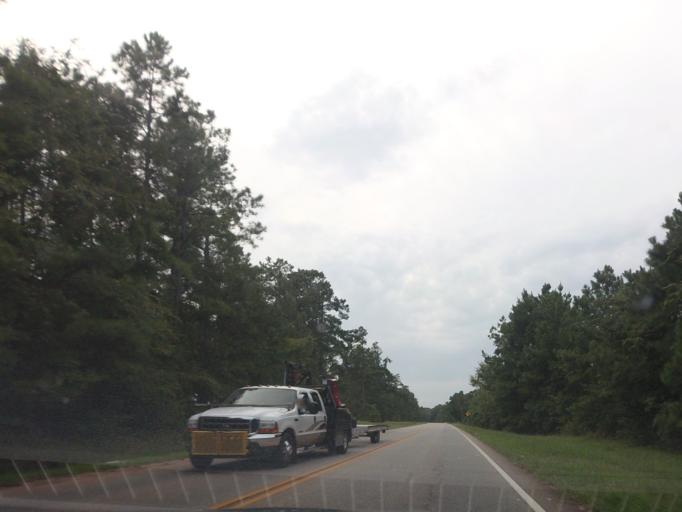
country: US
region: Georgia
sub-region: Twiggs County
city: Jeffersonville
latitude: 32.7117
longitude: -83.3849
